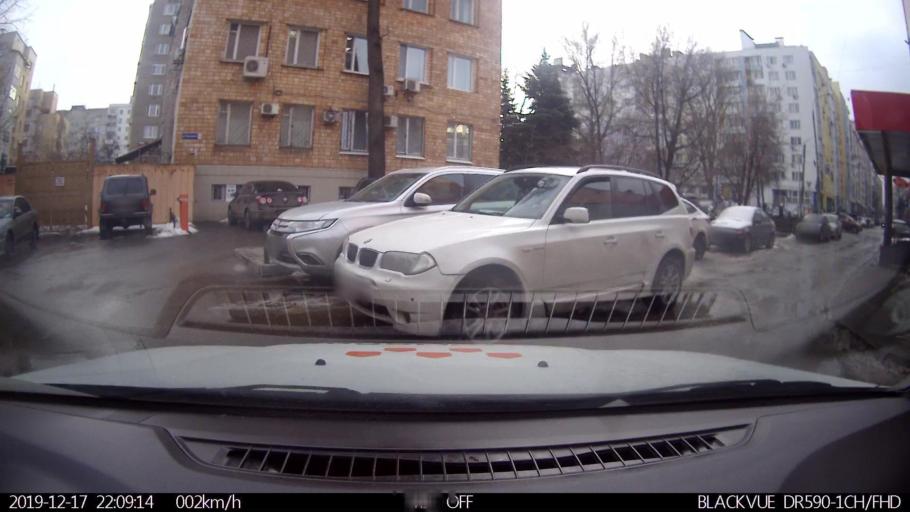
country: RU
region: Nizjnij Novgorod
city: Nizhniy Novgorod
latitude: 56.3174
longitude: 44.0250
